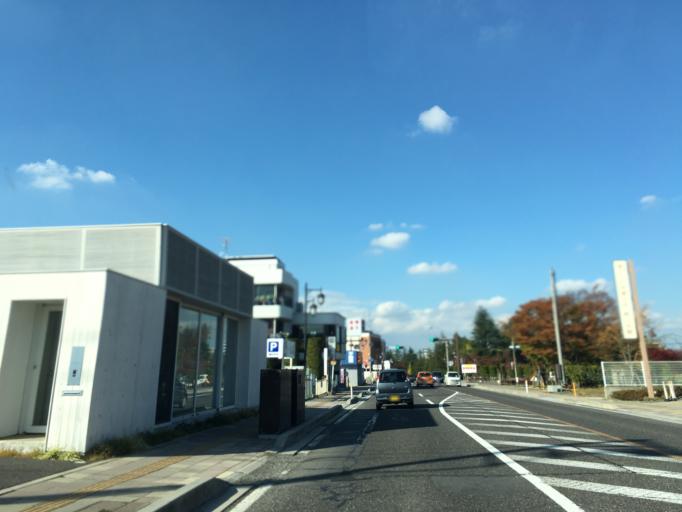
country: JP
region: Fukushima
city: Koriyama
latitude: 37.3939
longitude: 140.3549
